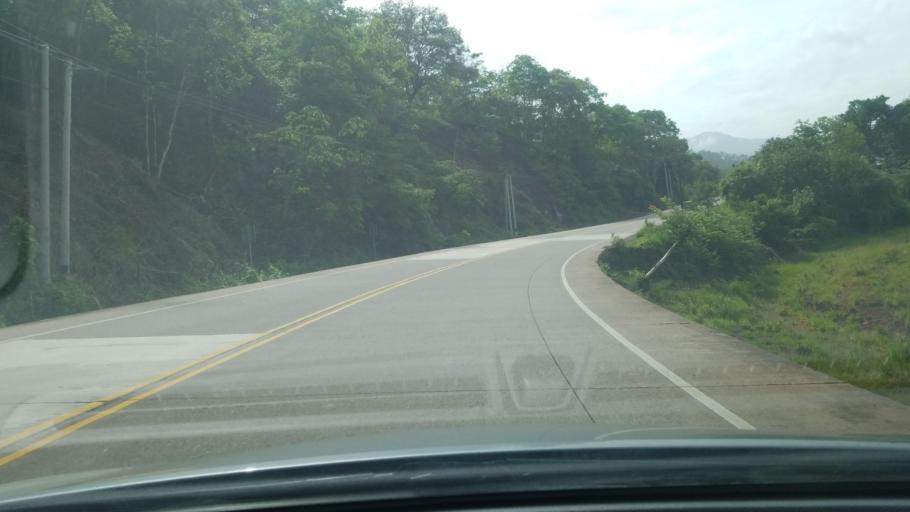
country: HN
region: Copan
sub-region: Santa Rita
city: Santa Rita, Copan
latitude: 14.8710
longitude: -89.0644
